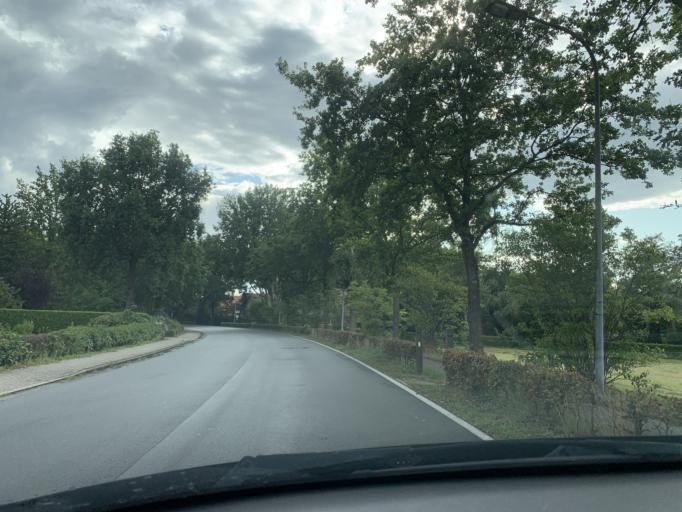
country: DE
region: Lower Saxony
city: Westerstede
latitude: 53.3125
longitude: 7.9178
